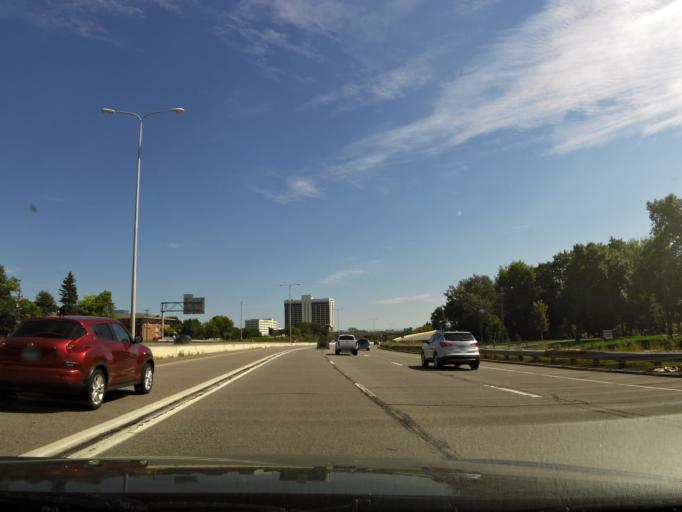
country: US
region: Minnesota
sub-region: Hennepin County
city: Minnetonka Mills
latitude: 44.9725
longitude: -93.4135
